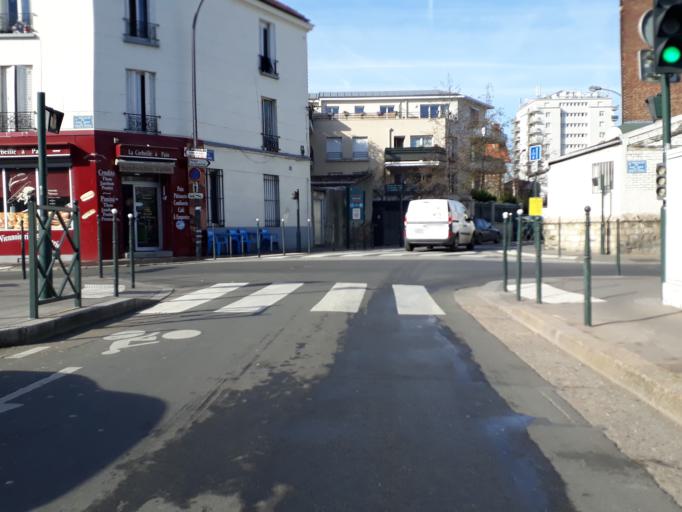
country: FR
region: Ile-de-France
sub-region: Departement des Hauts-de-Seine
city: Asnieres-sur-Seine
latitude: 48.9211
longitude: 2.2834
